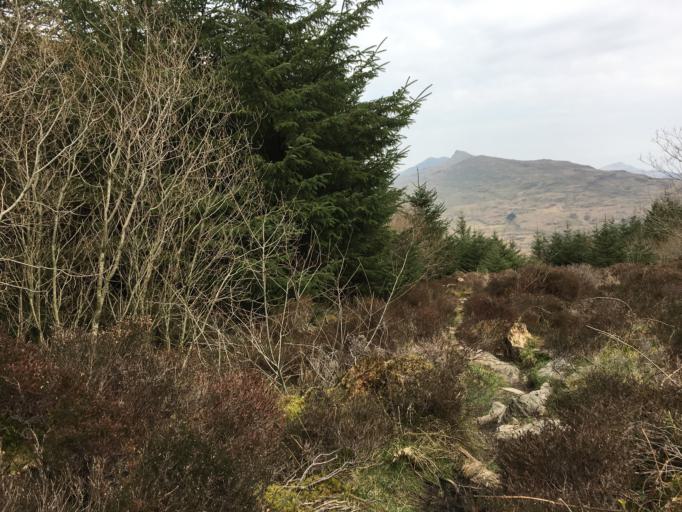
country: GB
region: Wales
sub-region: Gwynedd
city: Porthmadog
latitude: 53.0134
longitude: -4.1424
